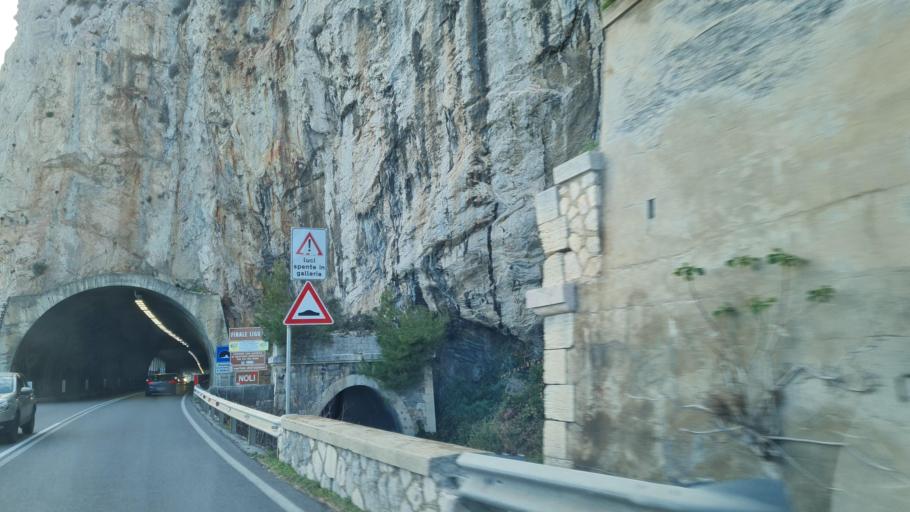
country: IT
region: Liguria
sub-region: Provincia di Savona
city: Noli
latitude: 44.1905
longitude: 8.4152
